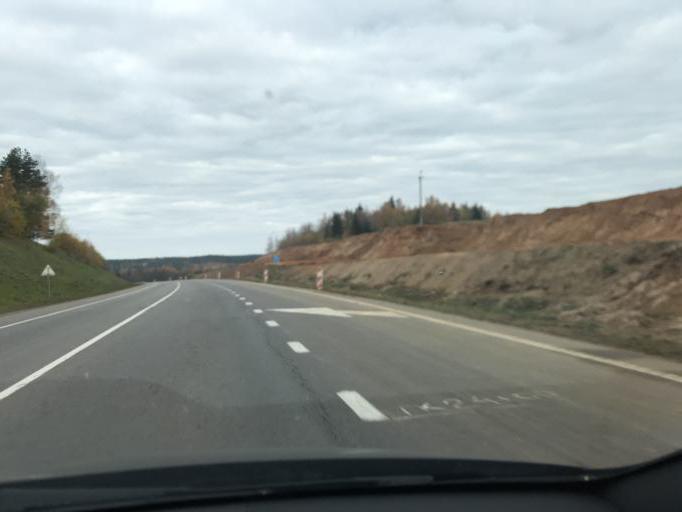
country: BY
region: Minsk
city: Slabada
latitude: 54.0315
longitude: 27.8683
